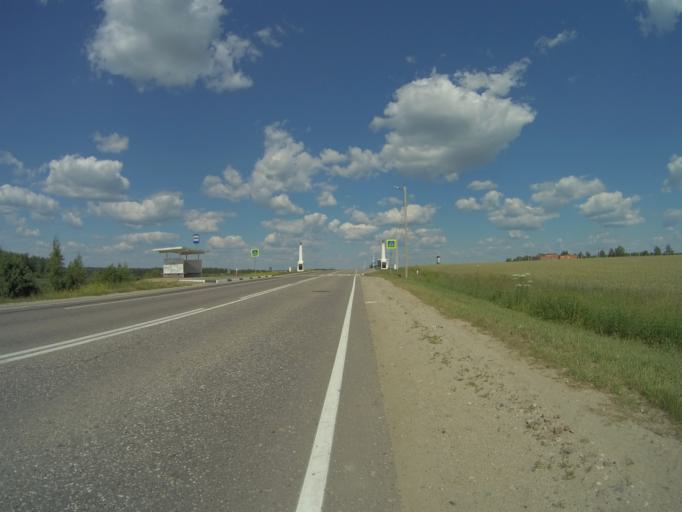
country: RU
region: Ivanovo
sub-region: Privolzhskiy Rayon
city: Ples
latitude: 57.4381
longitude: 41.4770
